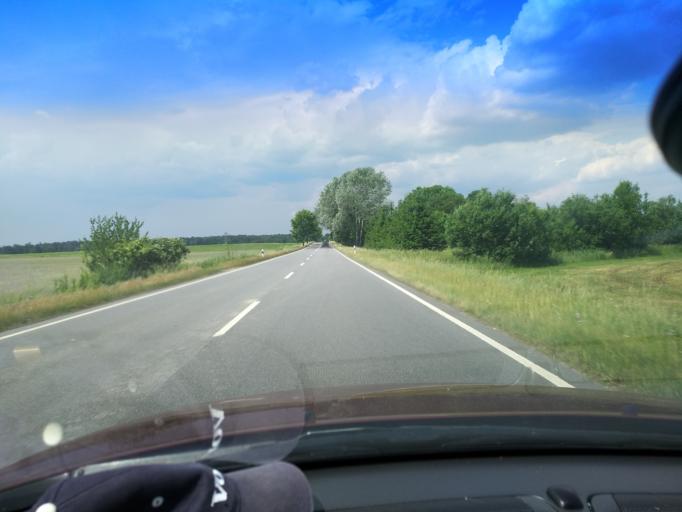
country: DE
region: Saxony
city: Niesky
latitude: 51.2715
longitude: 14.8404
